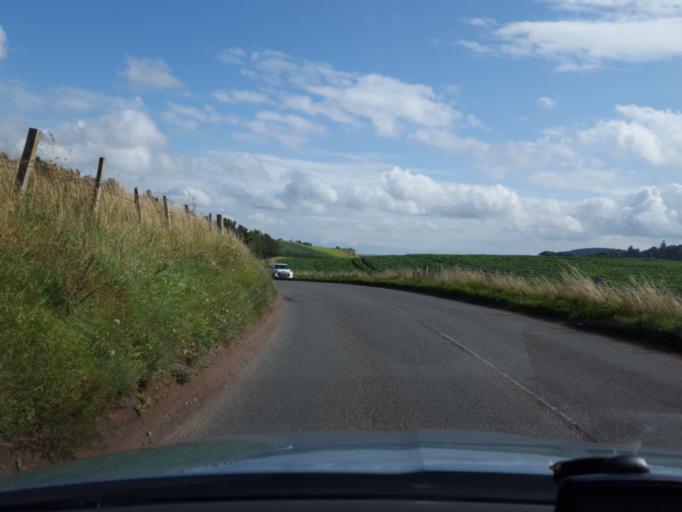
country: GB
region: Scotland
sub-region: Fife
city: Newport-On-Tay
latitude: 56.4150
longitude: -2.9738
